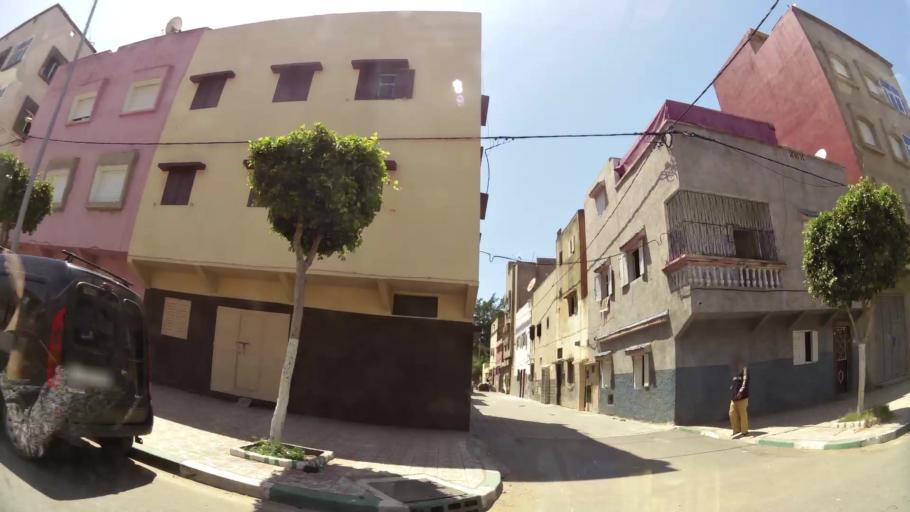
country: MA
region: Gharb-Chrarda-Beni Hssen
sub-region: Kenitra Province
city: Kenitra
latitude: 34.2574
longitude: -6.5605
